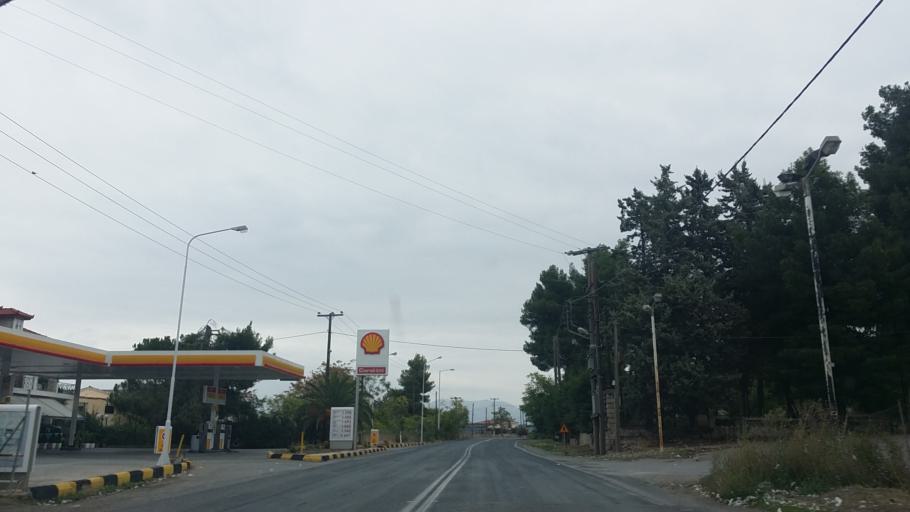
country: GR
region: Central Greece
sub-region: Nomos Voiotias
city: Thivai
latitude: 38.3270
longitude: 23.2994
